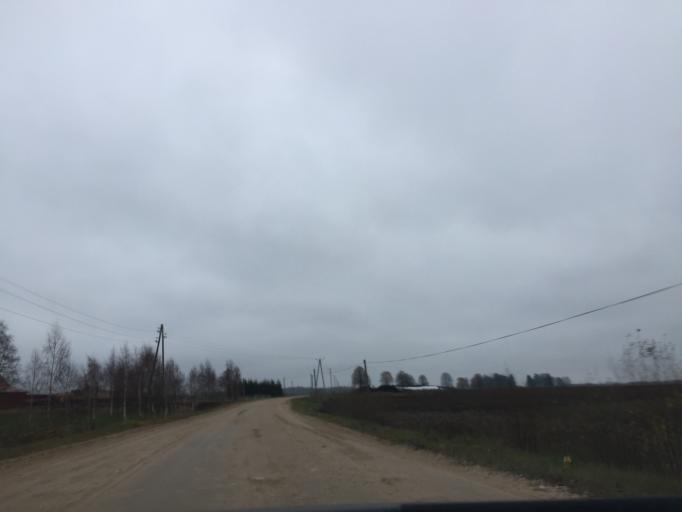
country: LV
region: Limbazu Rajons
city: Limbazi
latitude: 57.4289
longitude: 24.6648
